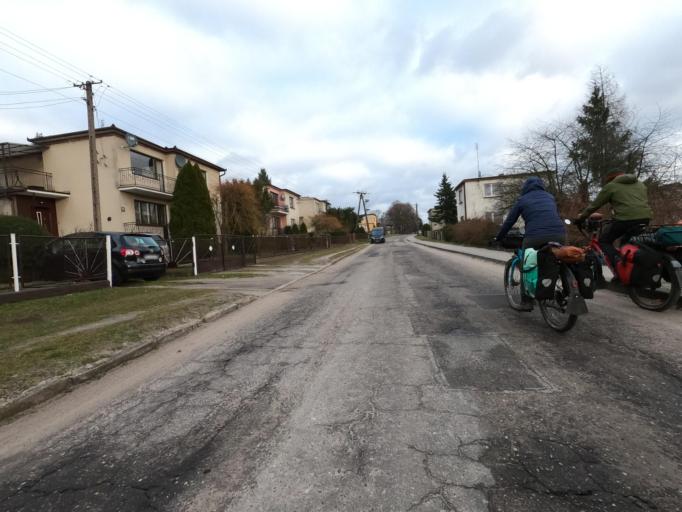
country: PL
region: Greater Poland Voivodeship
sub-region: Powiat pilski
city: Bialosliwie
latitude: 53.0985
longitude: 17.1134
